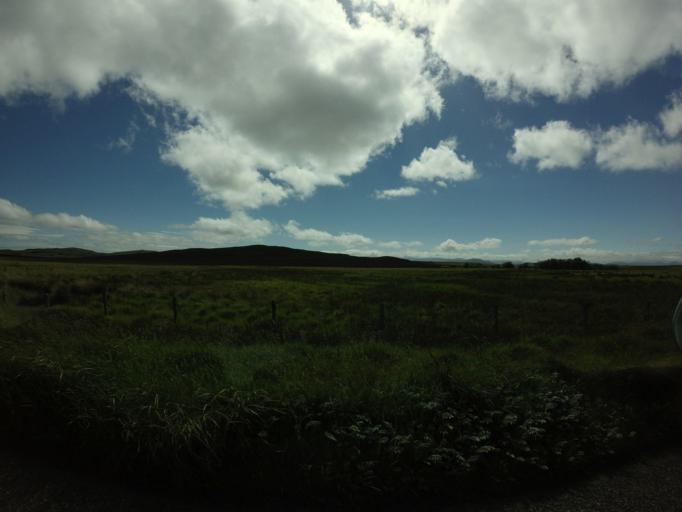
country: GB
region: Scotland
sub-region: Eilean Siar
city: Stornoway
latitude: 58.1645
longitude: -6.5421
